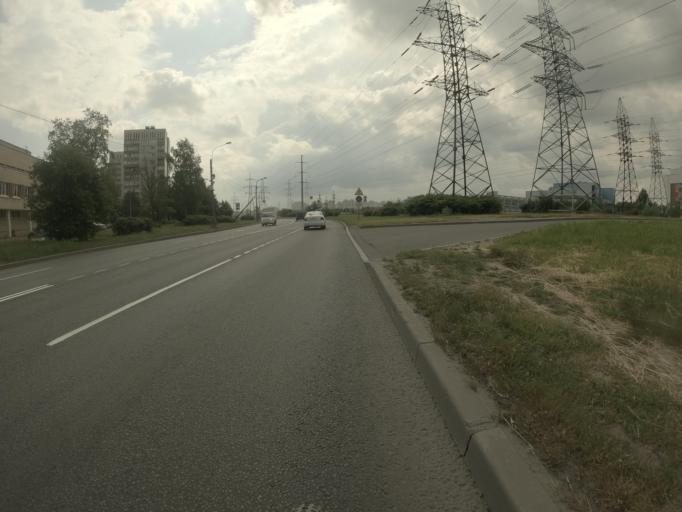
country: RU
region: St.-Petersburg
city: Krasnogvargeisky
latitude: 59.9468
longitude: 30.4609
